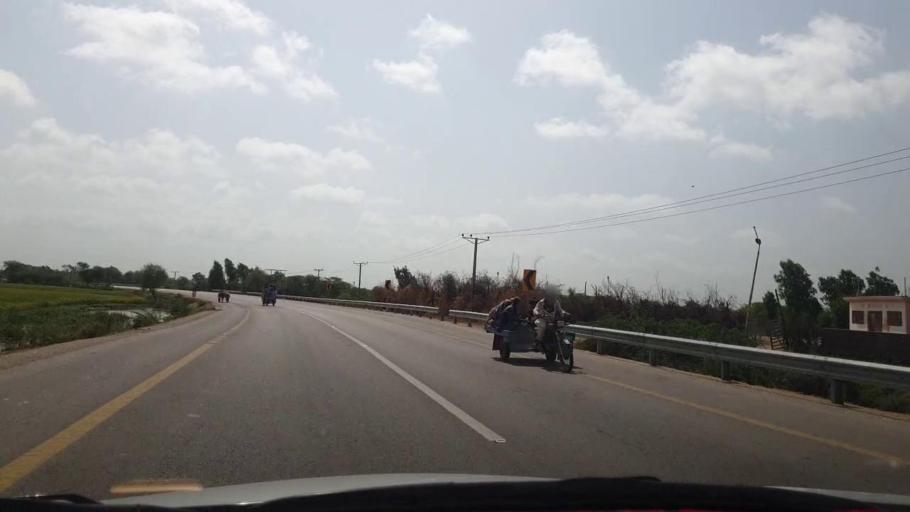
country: PK
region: Sindh
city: Talhar
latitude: 24.9108
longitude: 68.7325
